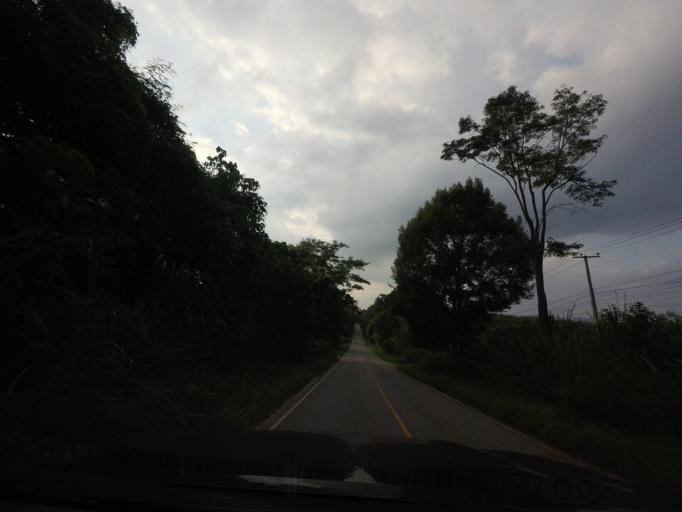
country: TH
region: Loei
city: Dan Sai
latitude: 17.3285
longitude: 101.1168
